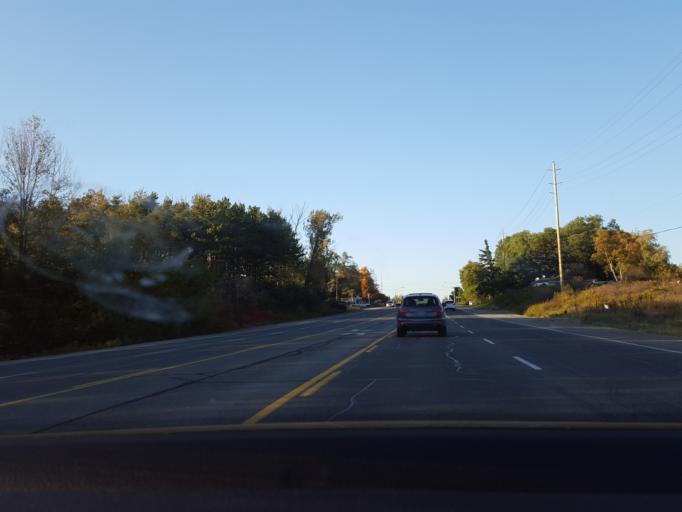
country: CA
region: Ontario
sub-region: York
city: Richmond Hill
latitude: 43.9560
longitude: -79.4572
